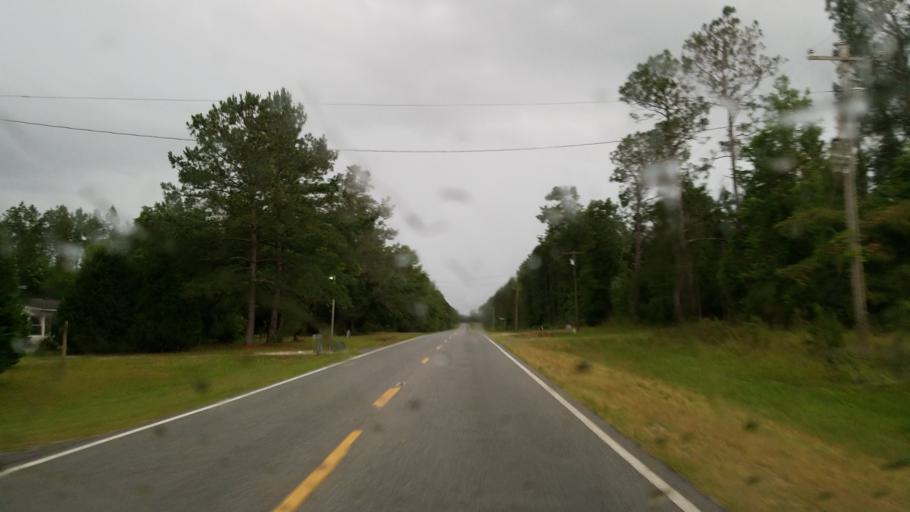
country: US
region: Georgia
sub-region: Lanier County
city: Lakeland
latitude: 30.9266
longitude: -83.0084
